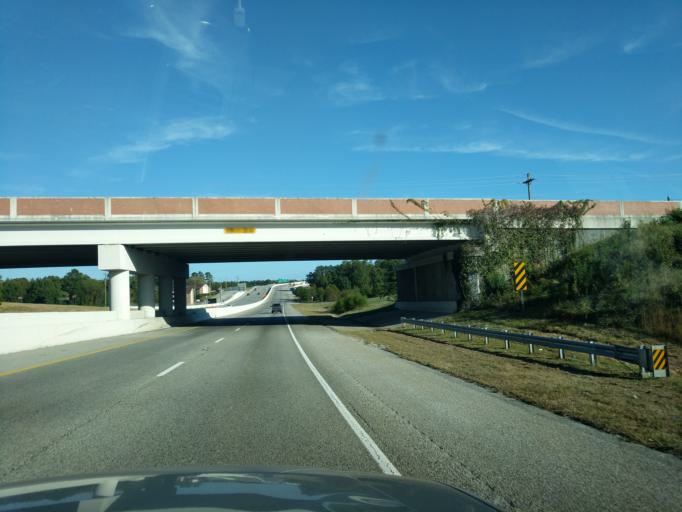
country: US
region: South Carolina
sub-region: Spartanburg County
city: Southern Shops
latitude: 34.9965
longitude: -81.9785
